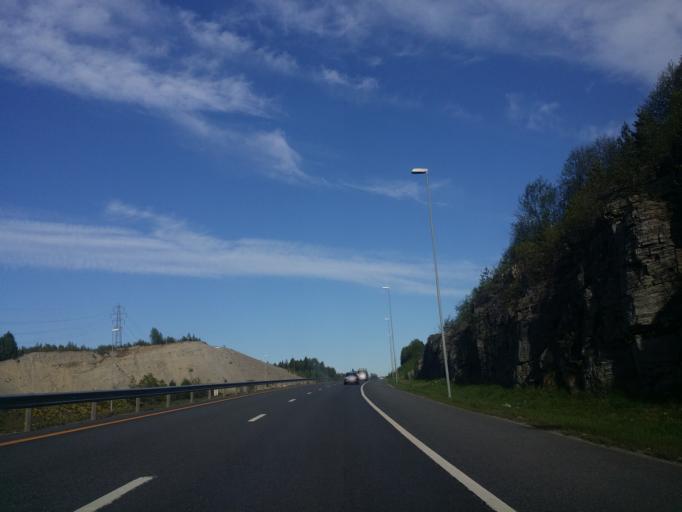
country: NO
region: Buskerud
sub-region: Nedre Eiker
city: Mjondalen
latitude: 59.7467
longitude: 10.0524
